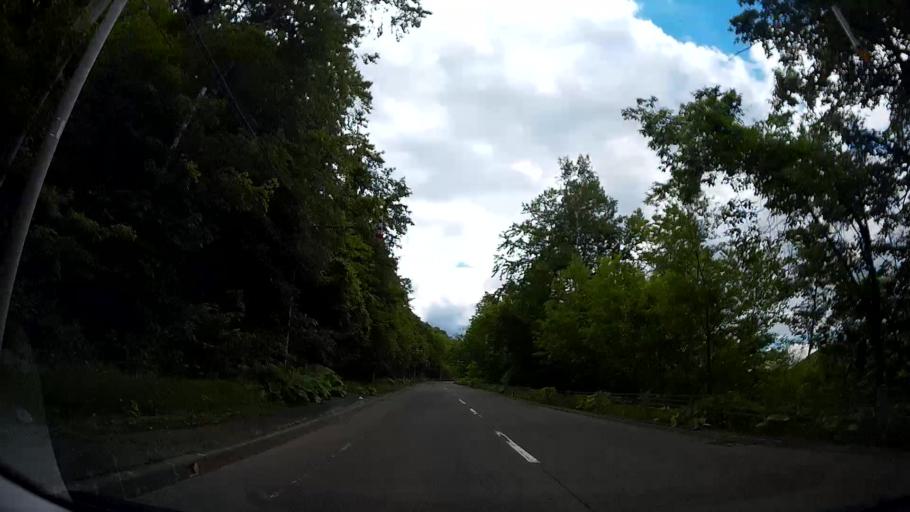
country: JP
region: Hokkaido
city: Kitahiroshima
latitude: 42.8450
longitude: 141.4364
